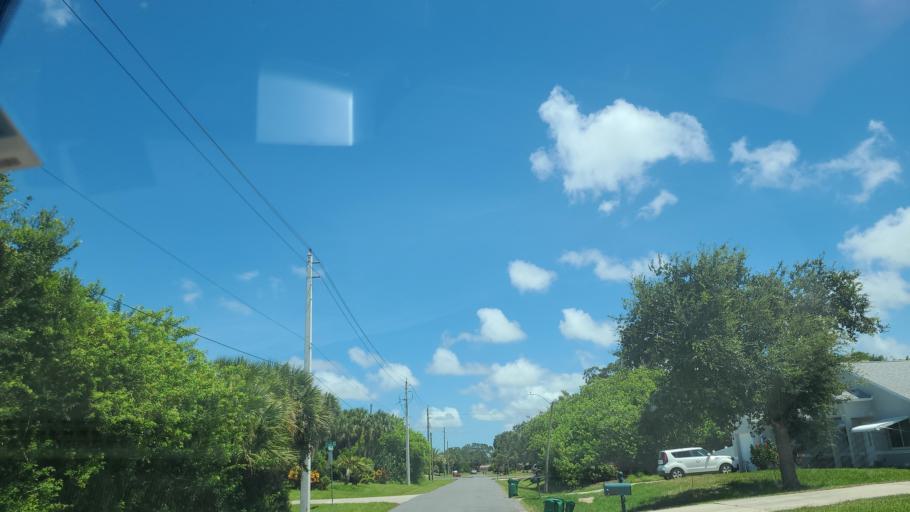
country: US
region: Florida
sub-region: Indian River County
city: Sebastian
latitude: 27.7819
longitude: -80.4824
